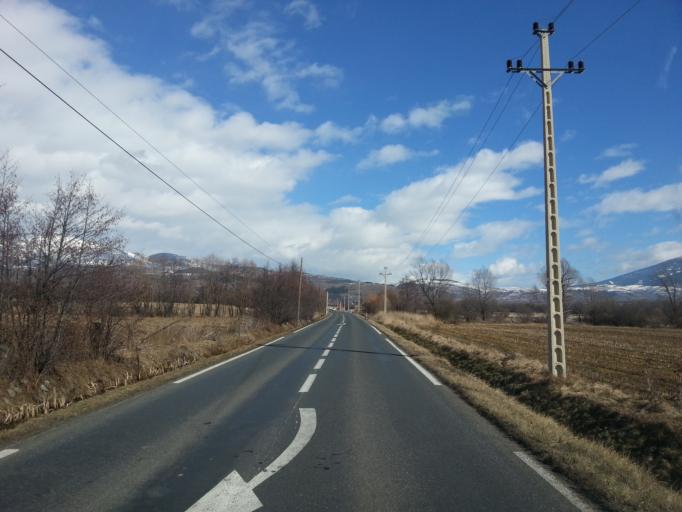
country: FR
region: Languedoc-Roussillon
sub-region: Departement des Pyrenees-Orientales
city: la Guingueta d'Ix
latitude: 42.4475
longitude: 1.9489
